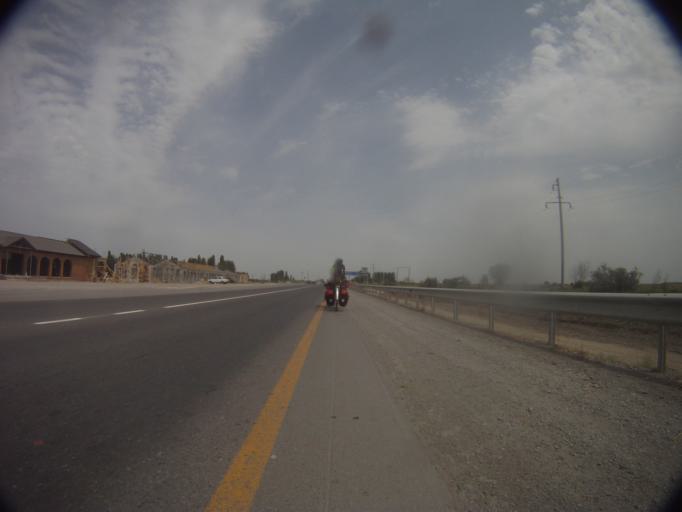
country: AZ
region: Ucar
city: Ujar
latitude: 40.5024
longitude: 47.5366
